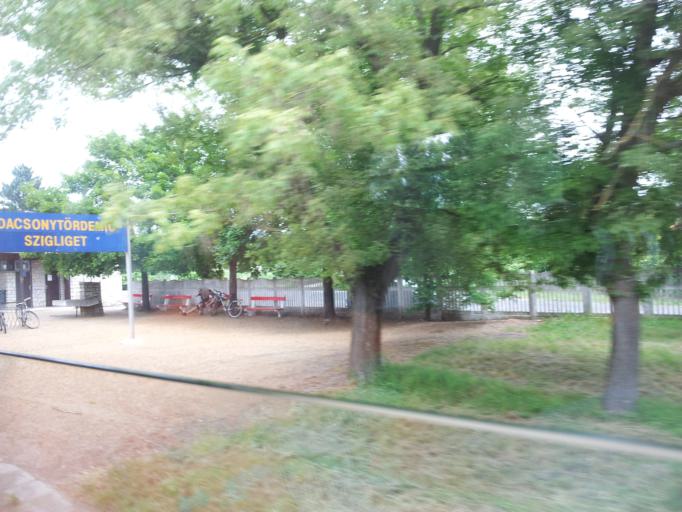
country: HU
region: Veszprem
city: Badacsonytomaj
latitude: 46.8094
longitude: 17.4691
